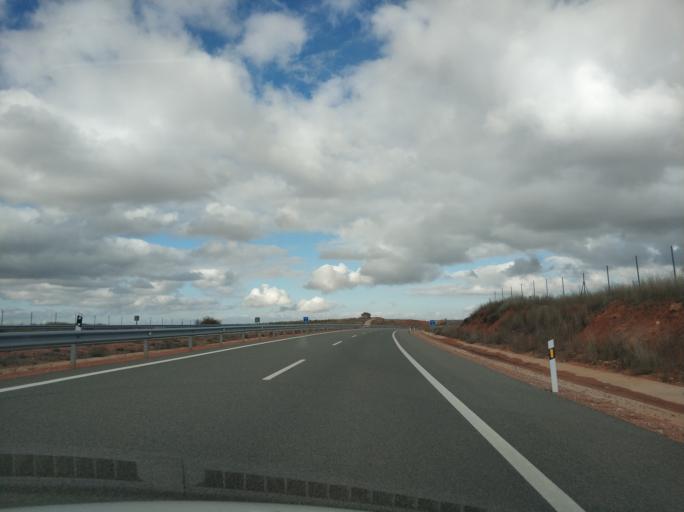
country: ES
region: Castille and Leon
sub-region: Provincia de Soria
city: Yelo
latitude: 41.2364
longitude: -2.4795
